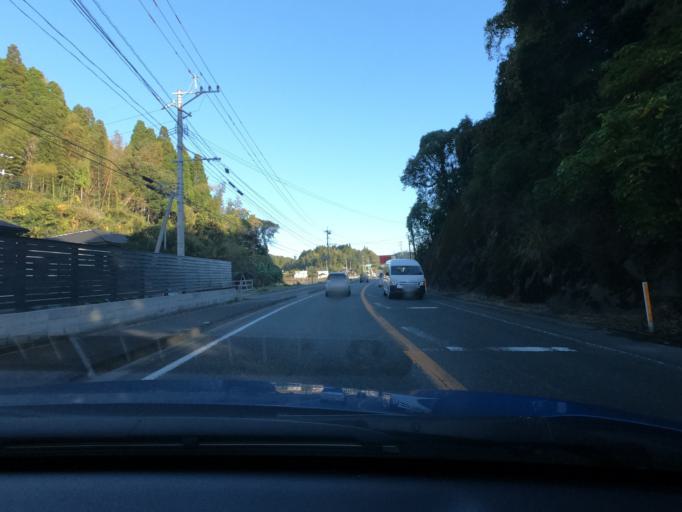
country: JP
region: Kagoshima
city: Satsumasendai
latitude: 31.8486
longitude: 130.2476
